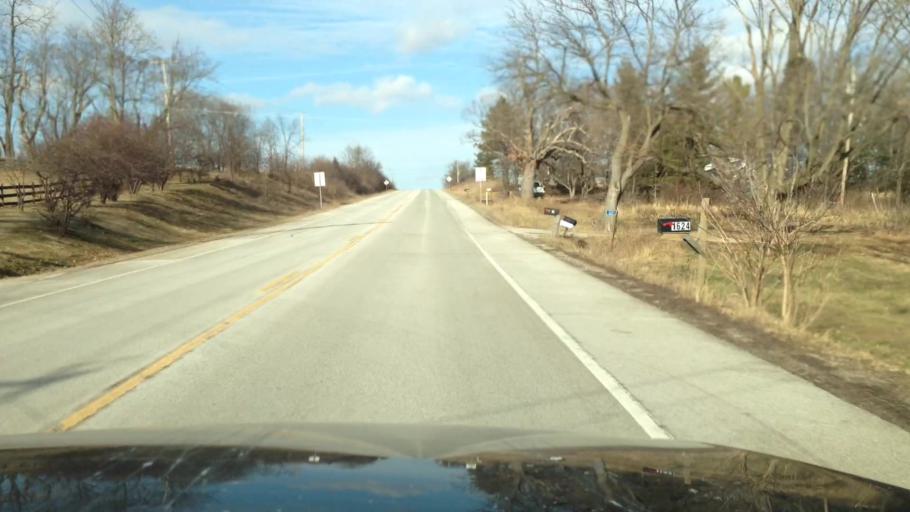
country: US
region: Wisconsin
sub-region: Walworth County
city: Lake Geneva
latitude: 42.6467
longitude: -88.4136
